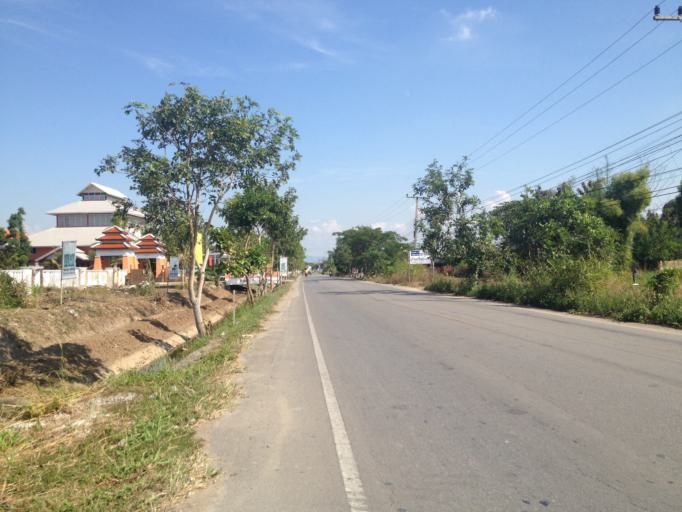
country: TH
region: Chiang Mai
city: Hang Dong
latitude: 18.6889
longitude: 98.9553
